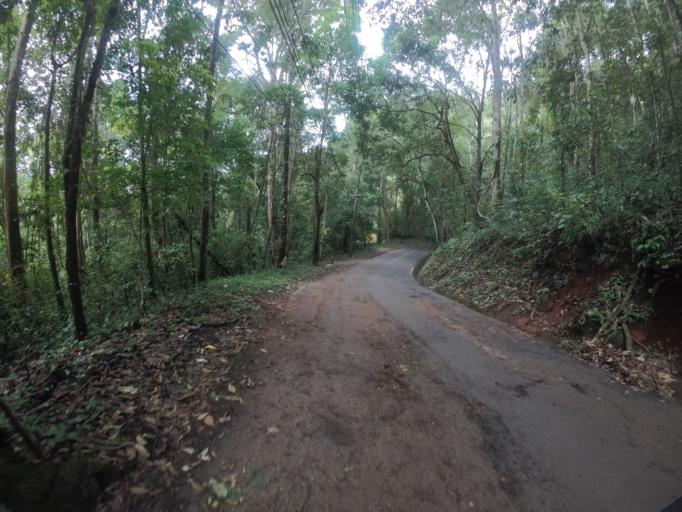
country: TH
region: Chiang Mai
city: Chiang Mai
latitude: 18.8105
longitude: 98.8900
